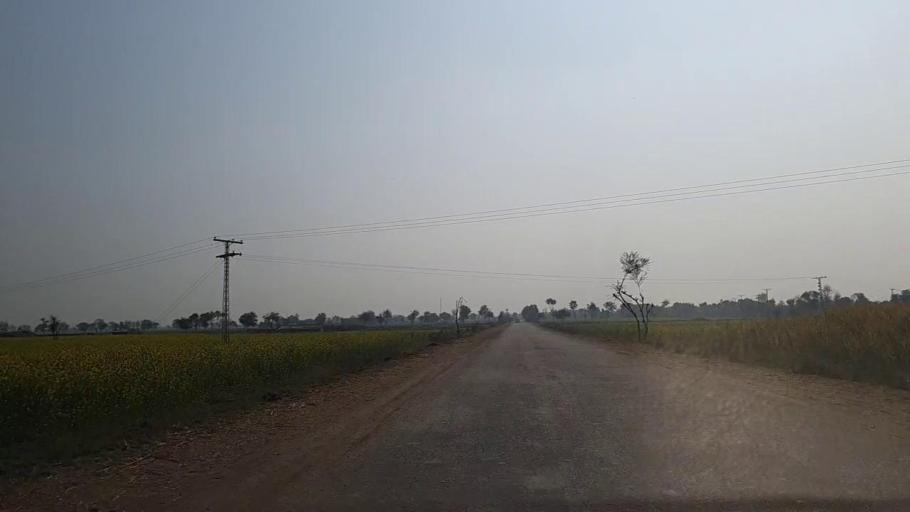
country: PK
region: Sindh
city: Jam Sahib
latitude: 26.3467
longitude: 68.5343
